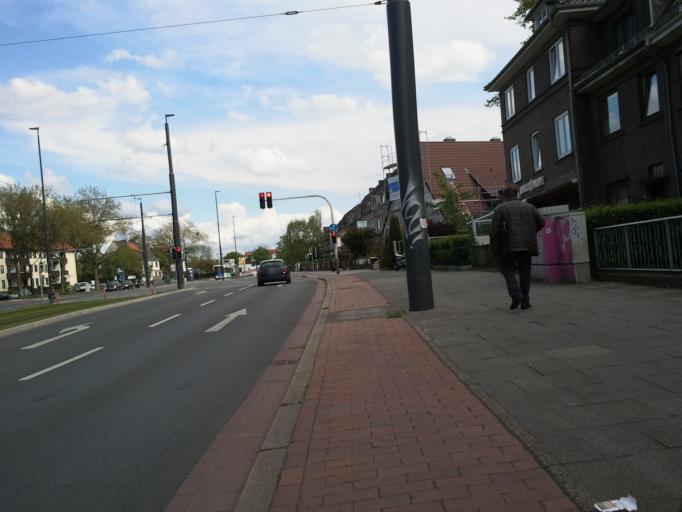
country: DE
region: Bremen
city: Bremen
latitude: 53.1062
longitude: 8.7778
